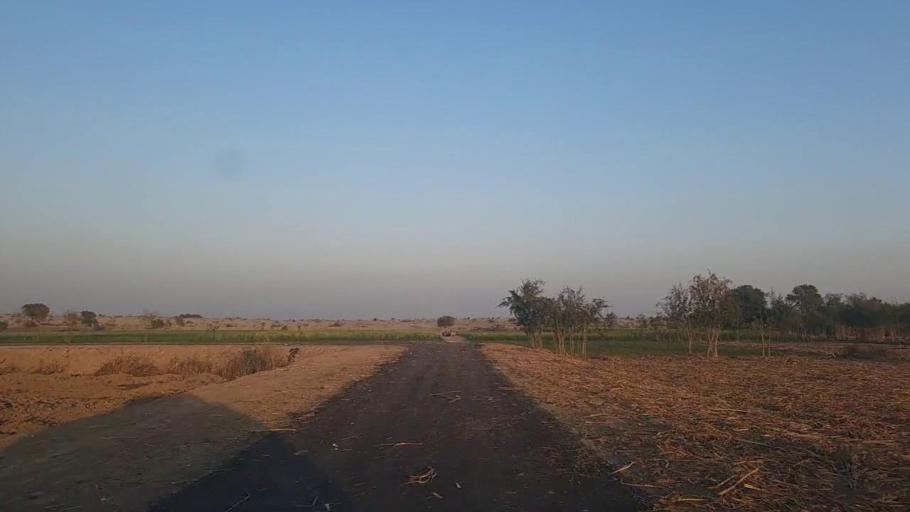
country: PK
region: Sindh
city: Jam Sahib
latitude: 26.3582
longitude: 68.7199
